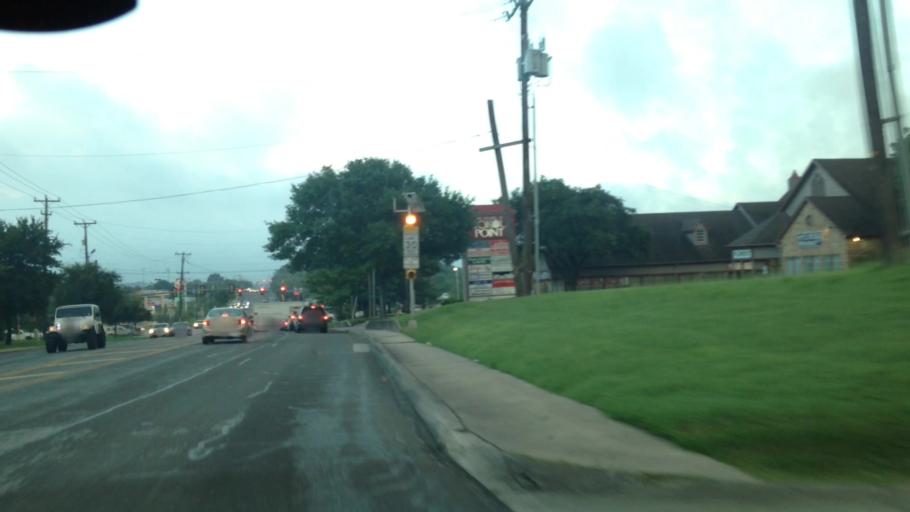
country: US
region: Texas
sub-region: Bexar County
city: Live Oak
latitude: 29.5794
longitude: -98.3735
